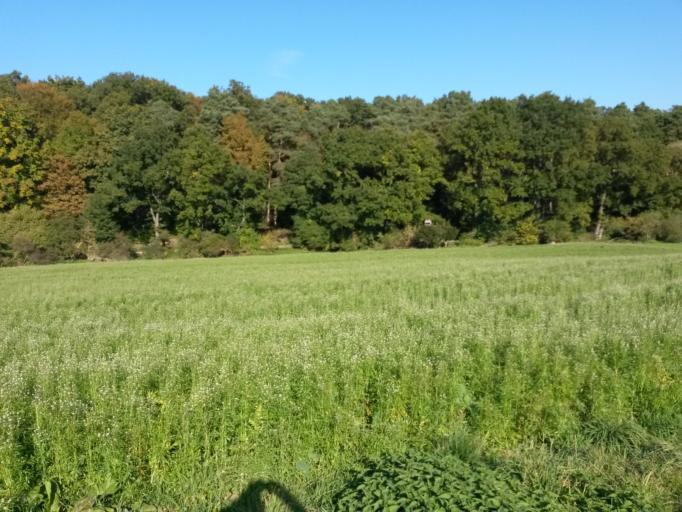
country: DE
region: Baden-Wuerttemberg
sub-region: Karlsruhe Region
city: Ettlingen
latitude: 48.9339
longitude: 8.5051
